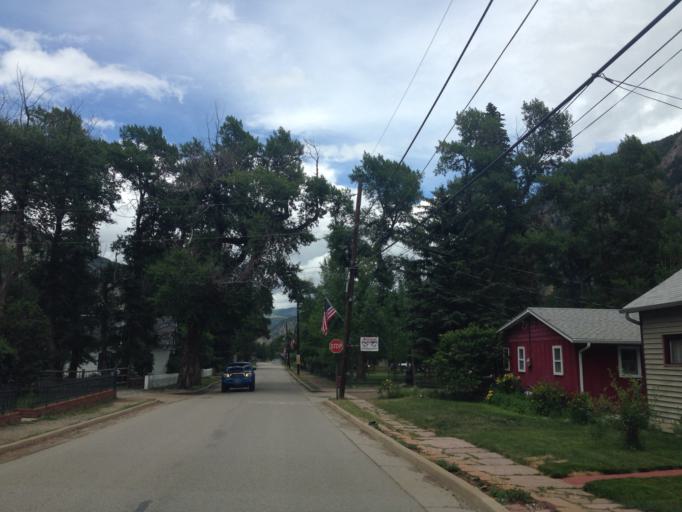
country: US
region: Colorado
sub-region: Clear Creek County
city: Georgetown
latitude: 39.7090
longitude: -105.6961
